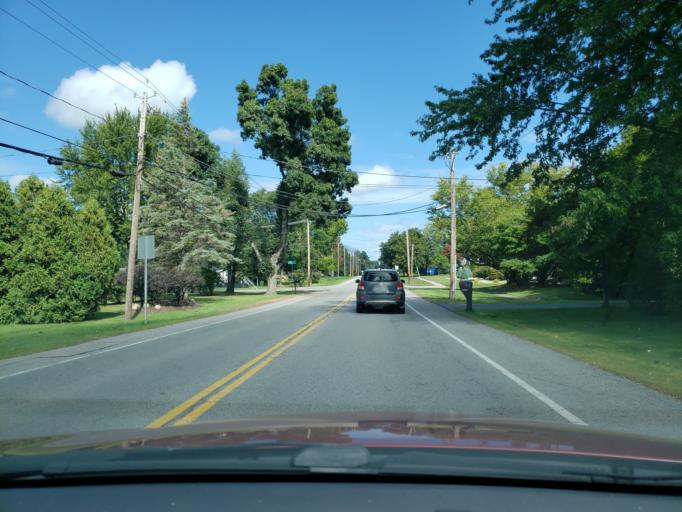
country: US
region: New York
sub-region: Monroe County
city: Greece
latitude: 43.2427
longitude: -77.7332
